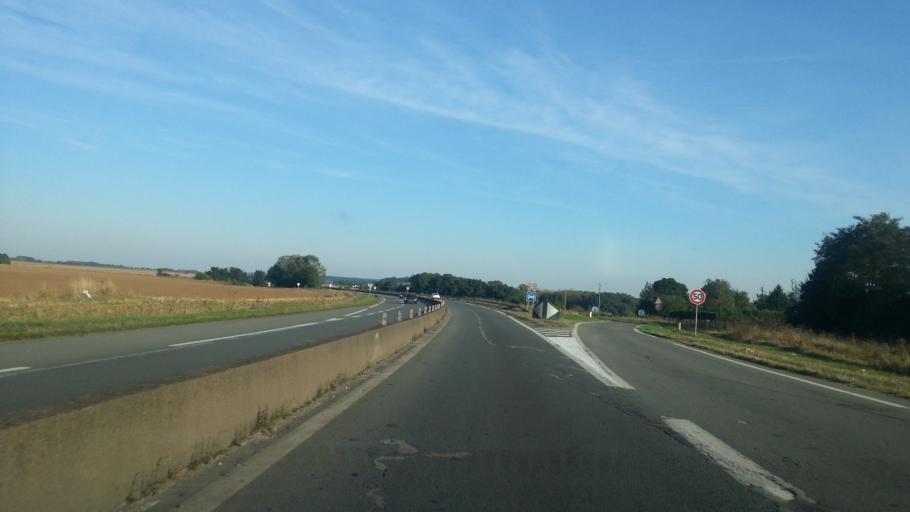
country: FR
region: Picardie
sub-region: Departement de l'Oise
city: Allonne
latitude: 49.4271
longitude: 2.1300
